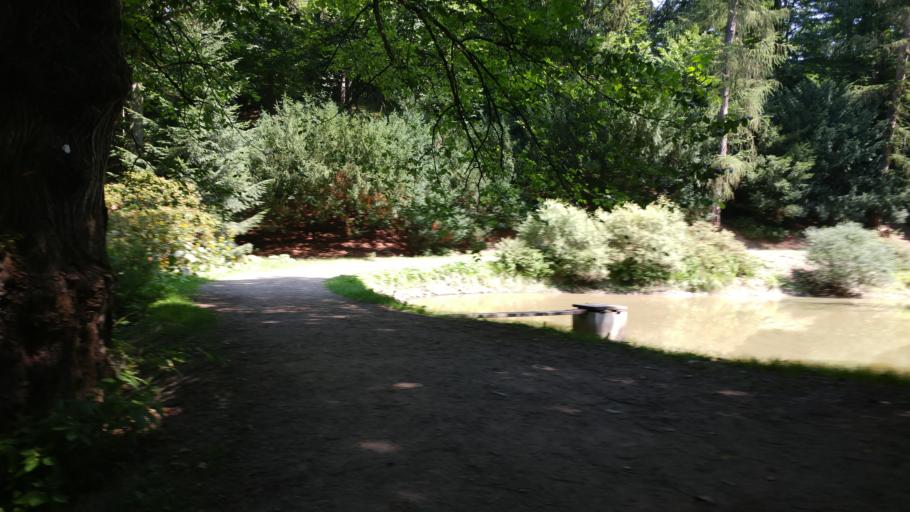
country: CZ
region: Central Bohemia
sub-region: Okres Praha-Zapad
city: Pruhonice
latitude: 49.9963
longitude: 14.5632
